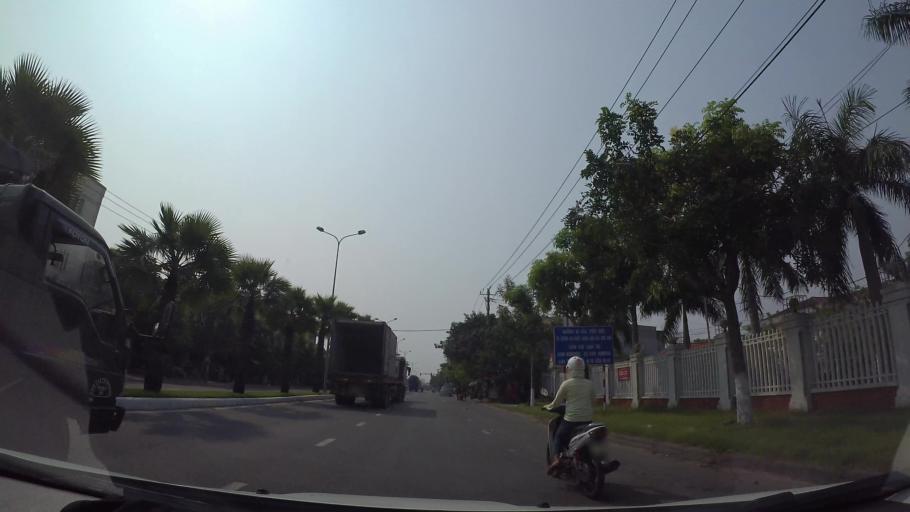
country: VN
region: Da Nang
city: Da Nang
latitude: 16.1070
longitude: 108.2462
